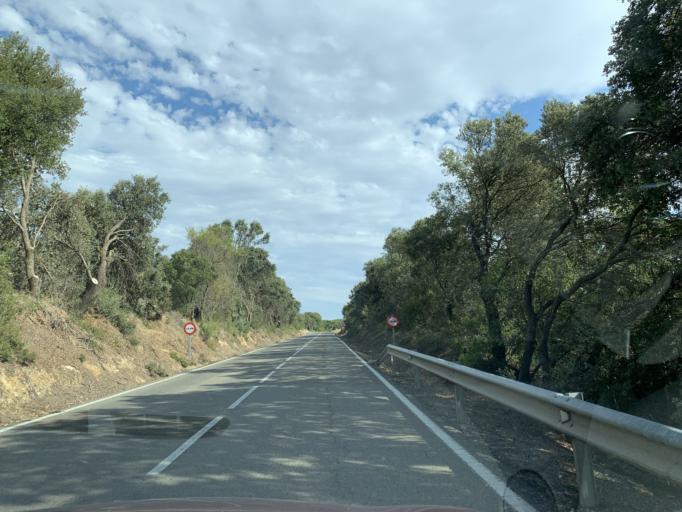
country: ES
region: Aragon
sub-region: Provincia de Zaragoza
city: Santa Eulalia de Gallego
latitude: 42.3077
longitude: -0.7471
